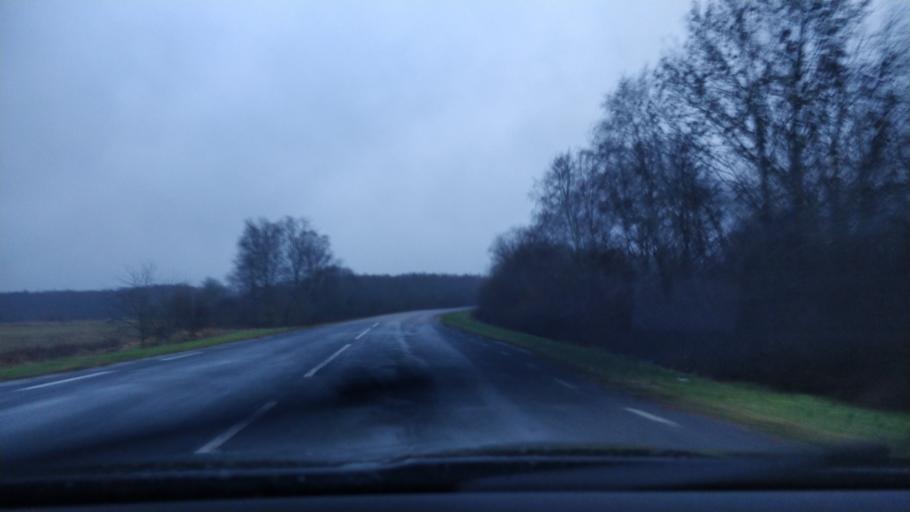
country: EE
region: Laeaene
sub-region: Lihula vald
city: Lihula
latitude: 58.7047
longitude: 23.8618
